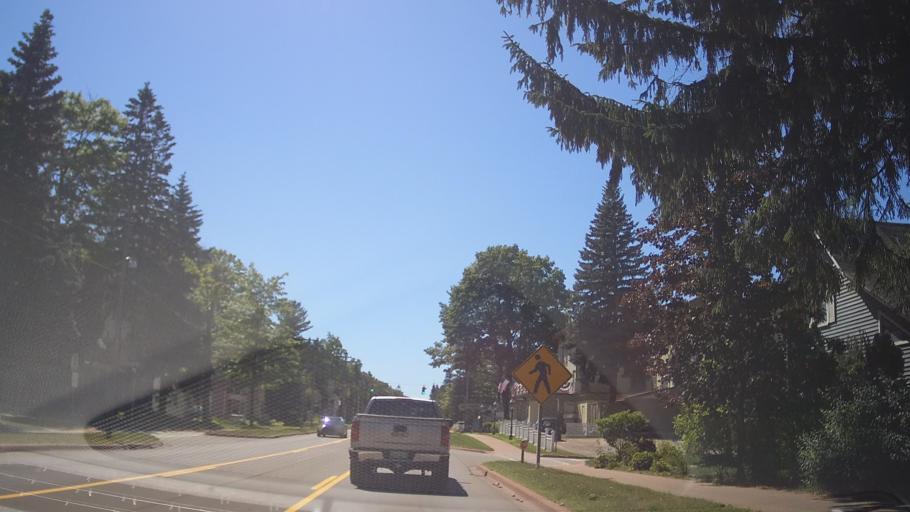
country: US
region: Michigan
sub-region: Emmet County
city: Petoskey
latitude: 45.3861
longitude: -84.9267
